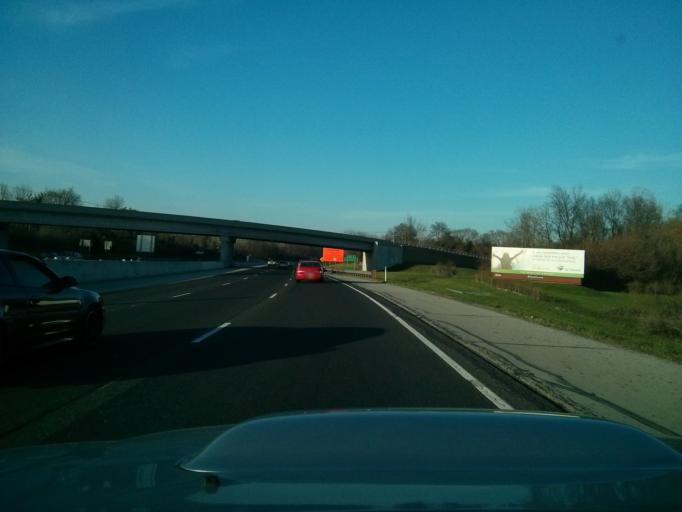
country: US
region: Indiana
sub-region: Marion County
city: Meridian Hills
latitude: 39.9261
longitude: -86.1794
